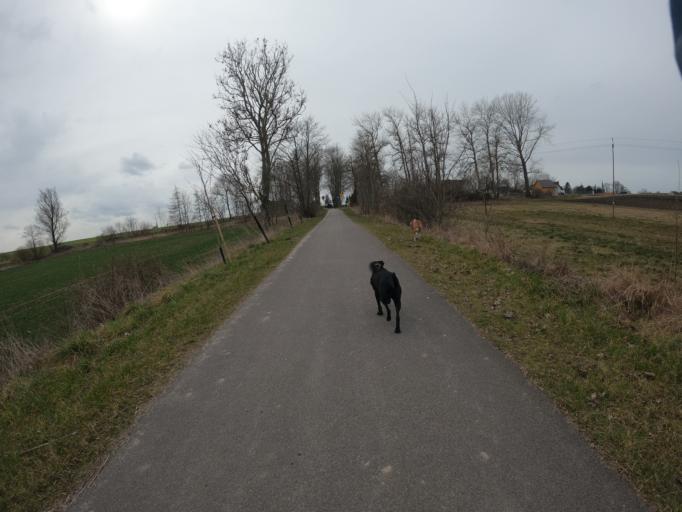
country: PL
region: West Pomeranian Voivodeship
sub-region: Powiat gryficki
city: Trzebiatow
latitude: 54.0914
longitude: 15.2716
